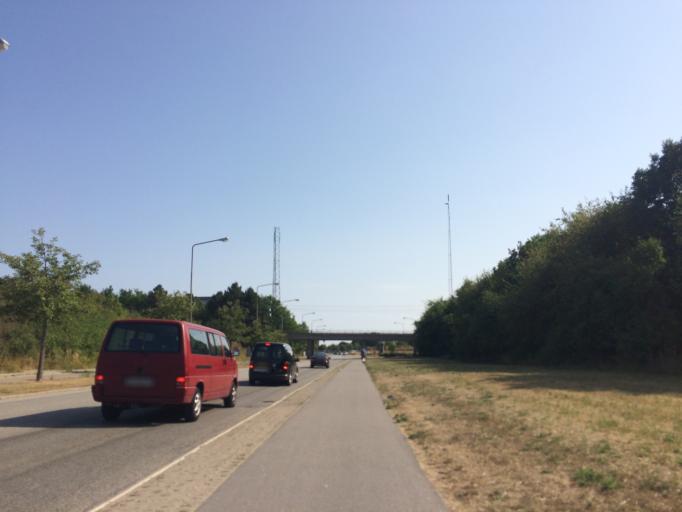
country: DK
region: Capital Region
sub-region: Hvidovre Kommune
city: Hvidovre
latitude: 55.6272
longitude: 12.4569
